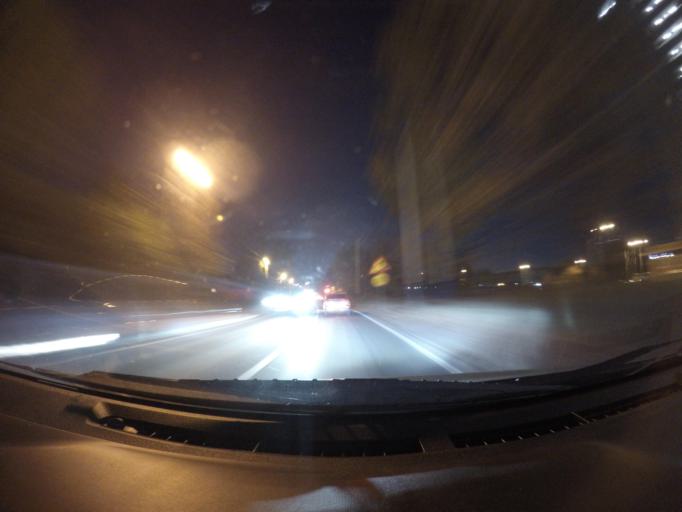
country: RU
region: Moskovskaya
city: Novopodrezkovo
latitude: 55.9217
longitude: 37.3758
